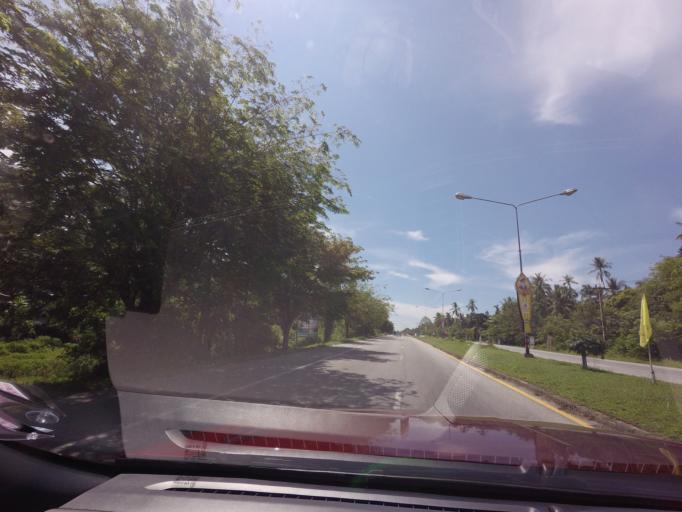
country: TH
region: Pattani
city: Mai Kaen
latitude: 6.6173
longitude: 101.6299
